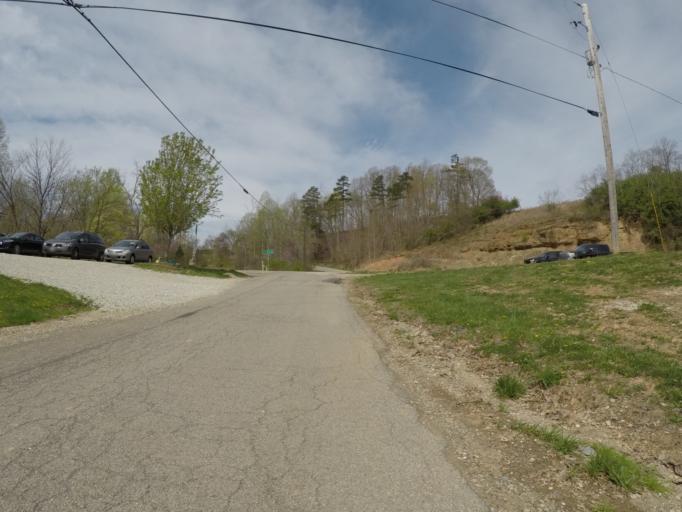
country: US
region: West Virginia
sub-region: Wayne County
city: Lavalette
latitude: 38.3542
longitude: -82.4032
